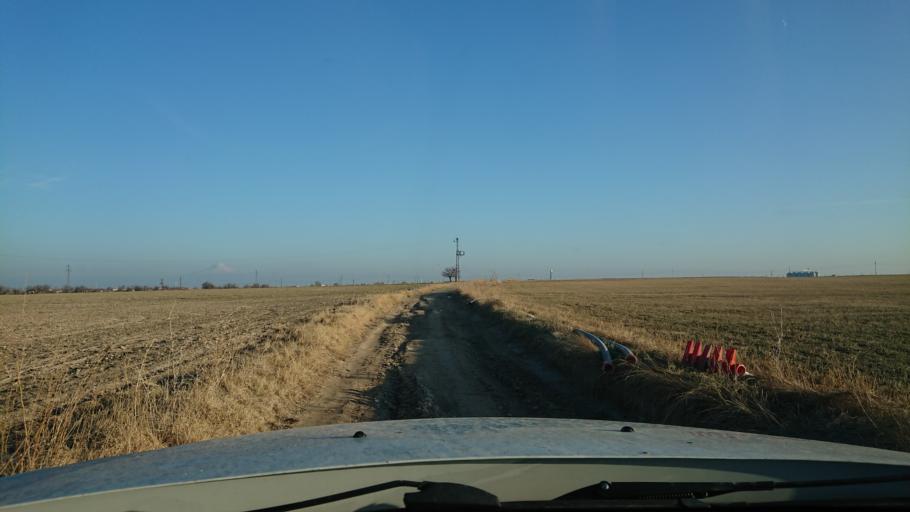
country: TR
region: Aksaray
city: Sultanhani
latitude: 38.2700
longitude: 33.5169
